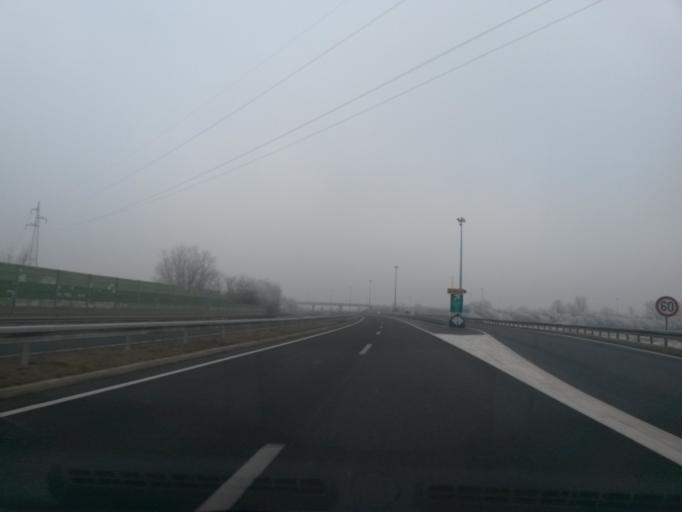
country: HR
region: Zagrebacka
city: Brckovljani
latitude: 45.9004
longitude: 16.2678
